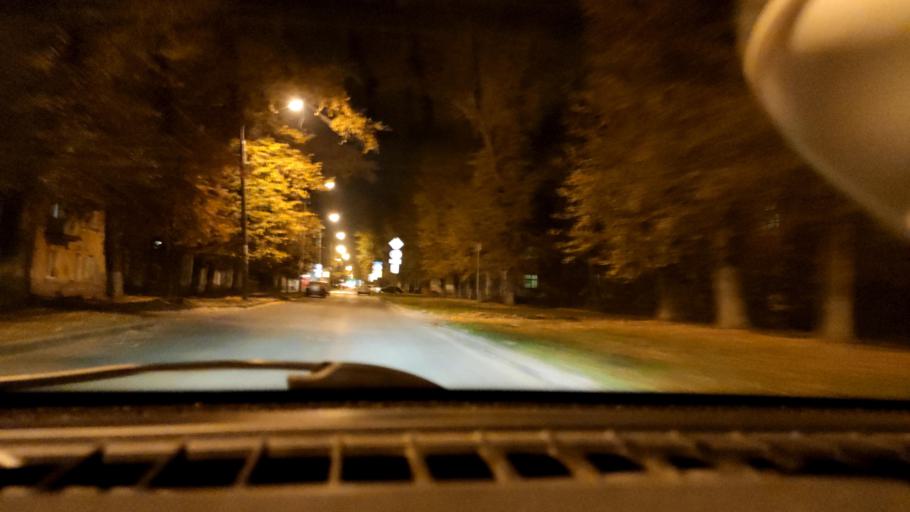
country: RU
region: Samara
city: Samara
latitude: 53.2196
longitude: 50.2540
